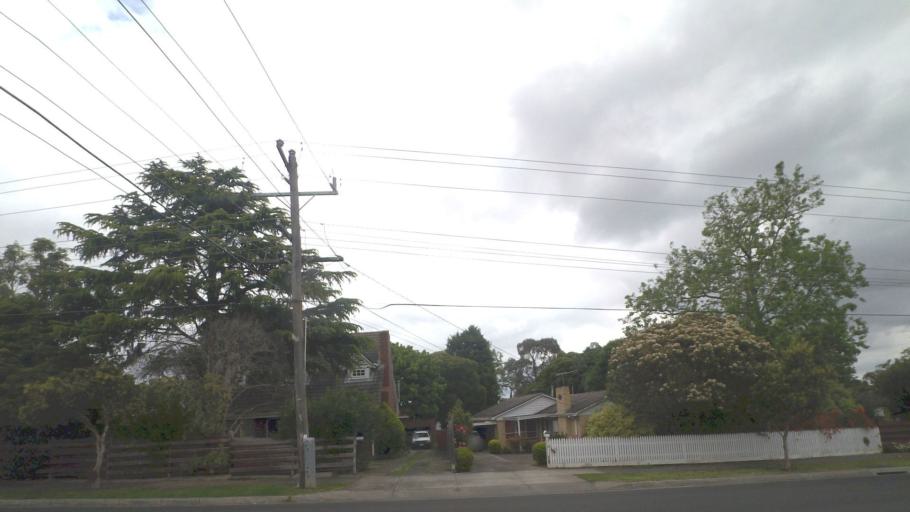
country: AU
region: Victoria
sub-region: Maroondah
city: Heathmont
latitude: -37.8485
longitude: 145.2514
